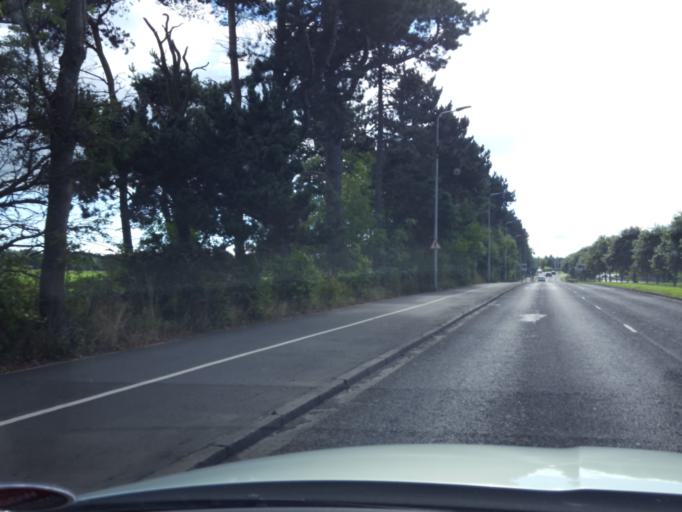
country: GB
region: Scotland
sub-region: Fife
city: Rosyth
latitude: 56.0528
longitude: -3.4343
